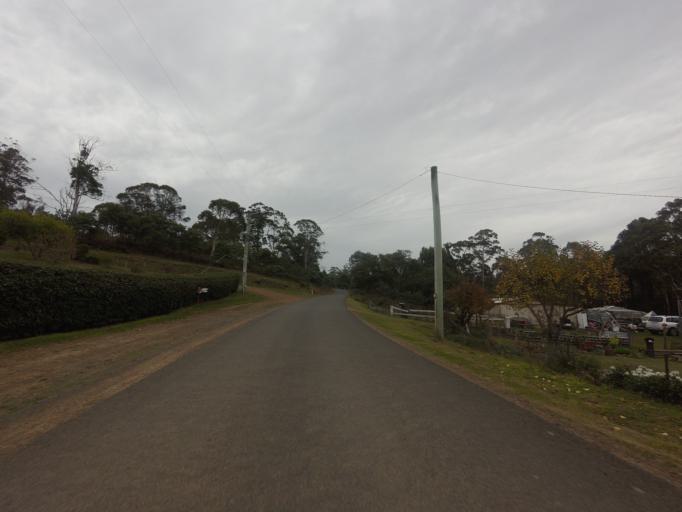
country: AU
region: Tasmania
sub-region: Derwent Valley
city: New Norfolk
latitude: -42.5796
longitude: 147.0052
